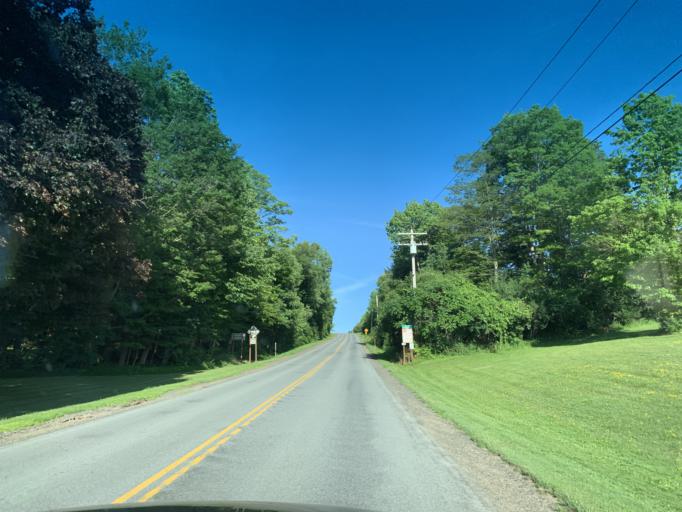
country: US
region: New York
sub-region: Oneida County
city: Vernon
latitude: 43.0555
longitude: -75.4606
